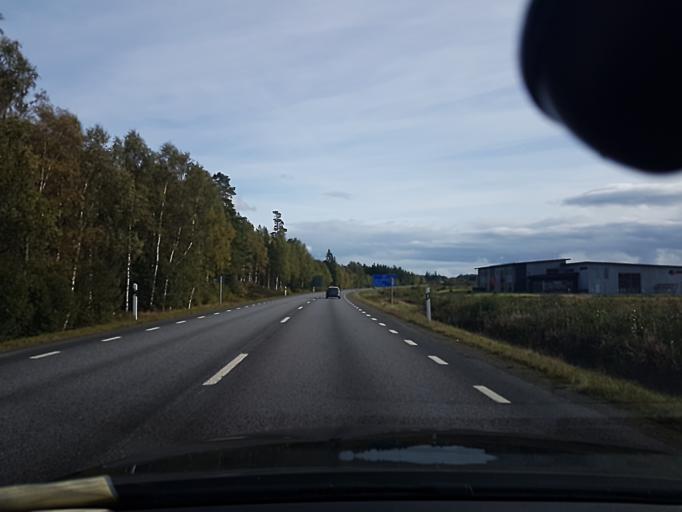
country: SE
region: Joenkoeping
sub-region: Varnamo Kommun
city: Varnamo
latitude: 57.1626
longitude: 14.0784
